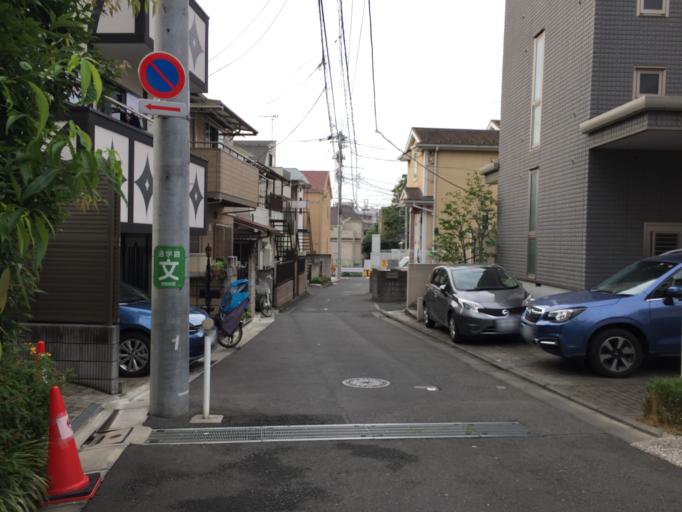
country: JP
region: Tokyo
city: Tokyo
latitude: 35.6501
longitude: 139.6716
